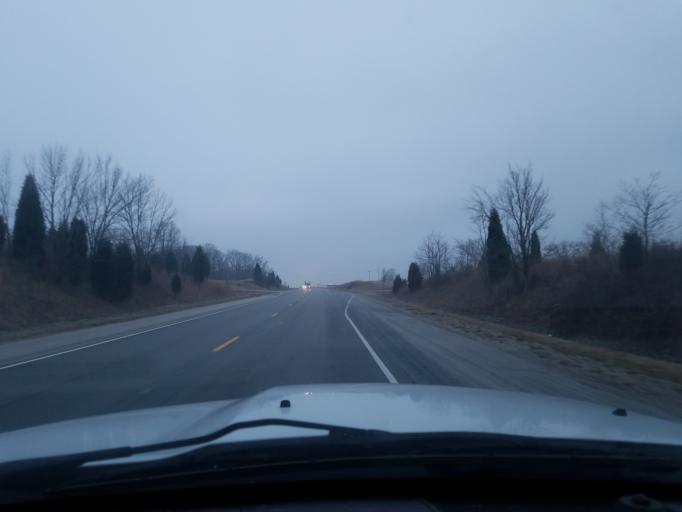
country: US
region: Indiana
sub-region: Crawford County
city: English
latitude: 38.1759
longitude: -86.6042
